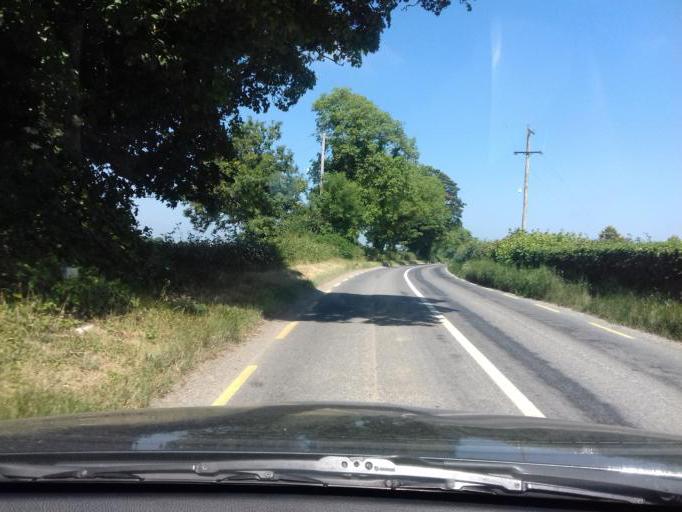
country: IE
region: Leinster
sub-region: An Mhi
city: Stamullin
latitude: 53.5850
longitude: -6.2997
